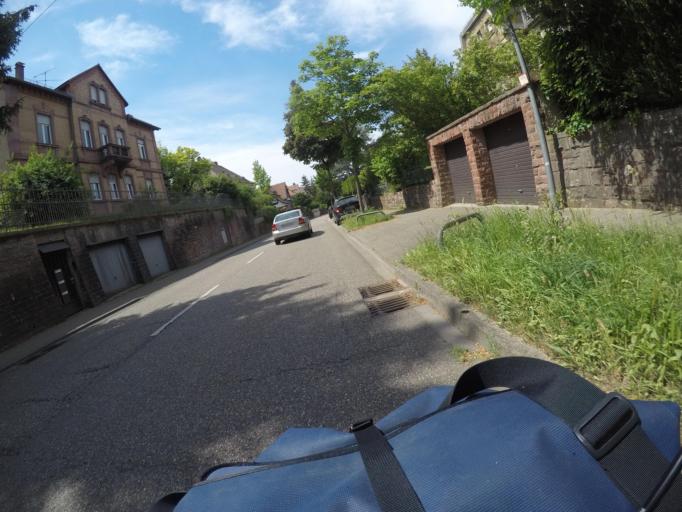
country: DE
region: Baden-Wuerttemberg
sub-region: Karlsruhe Region
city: Weingarten
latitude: 48.9954
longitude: 8.4798
